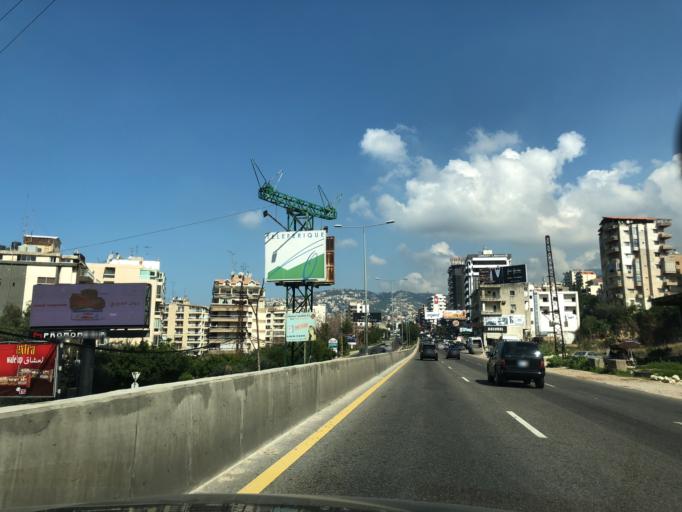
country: LB
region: Mont-Liban
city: Djounie
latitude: 33.9910
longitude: 35.6430
